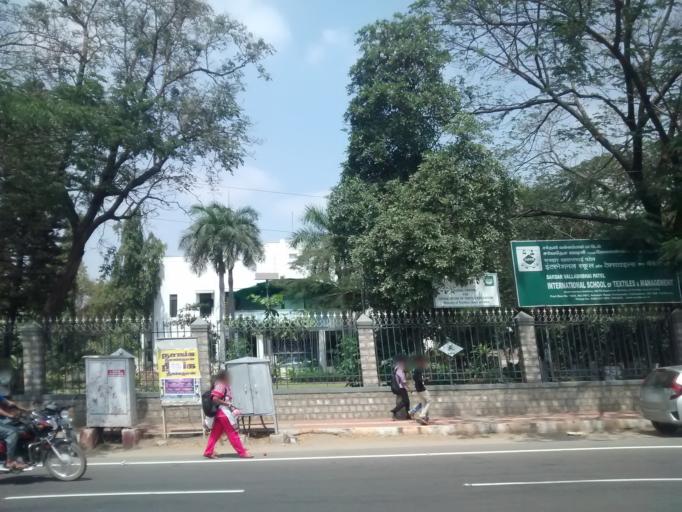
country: IN
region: Tamil Nadu
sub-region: Coimbatore
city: Singanallur
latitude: 11.0246
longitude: 77.0082
